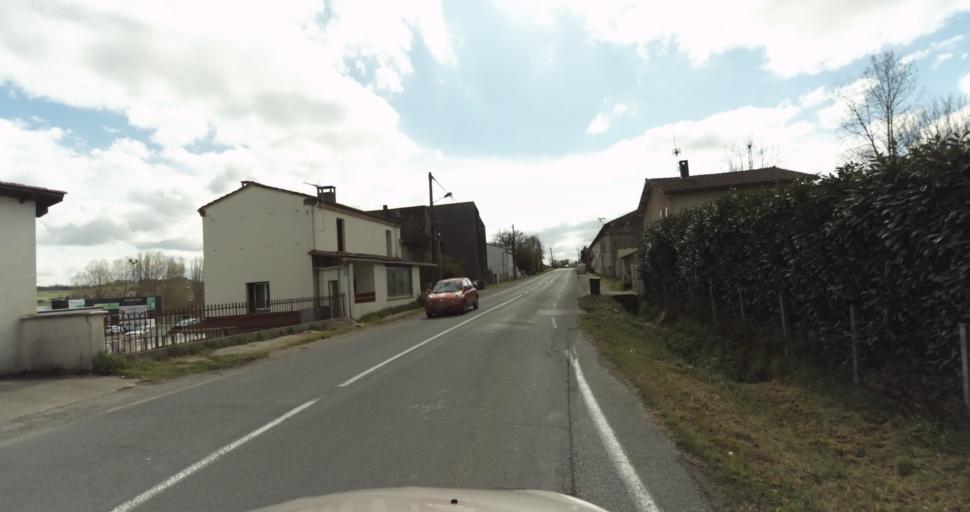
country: FR
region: Midi-Pyrenees
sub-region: Departement du Tarn
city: Puygouzon
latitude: 43.8980
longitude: 2.1495
